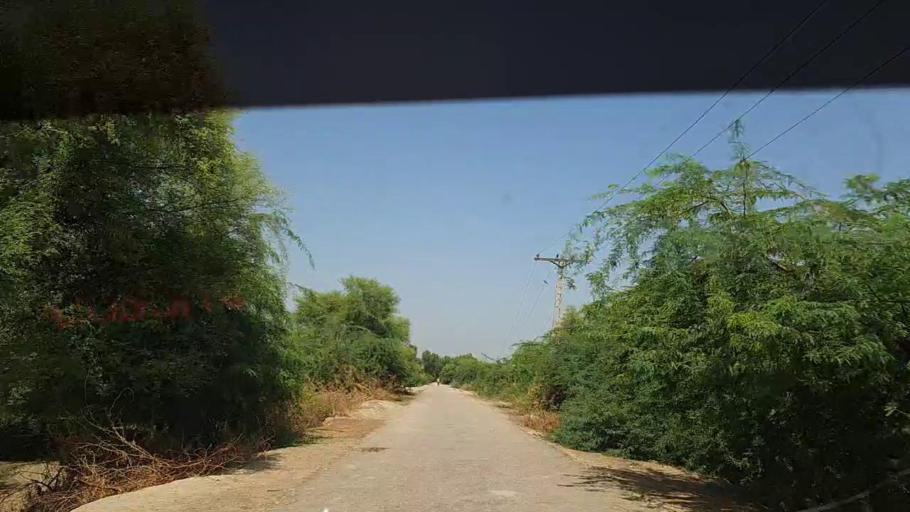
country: PK
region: Sindh
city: Ghauspur
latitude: 28.1652
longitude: 69.1393
